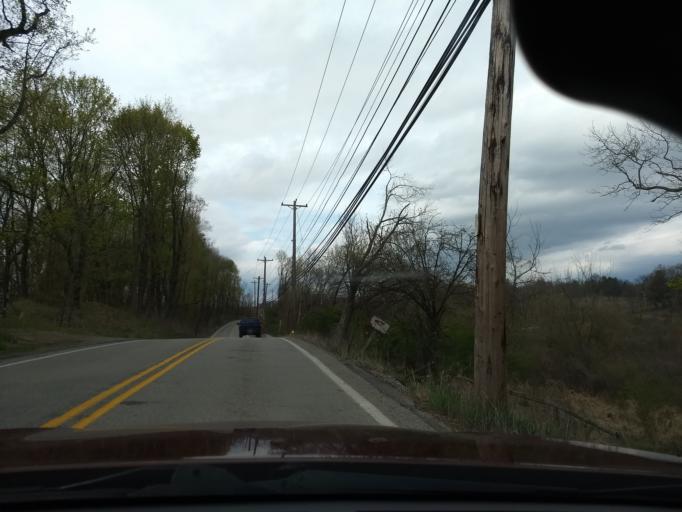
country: US
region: Pennsylvania
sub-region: Allegheny County
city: Fox Chapel
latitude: 40.5488
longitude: -79.9002
